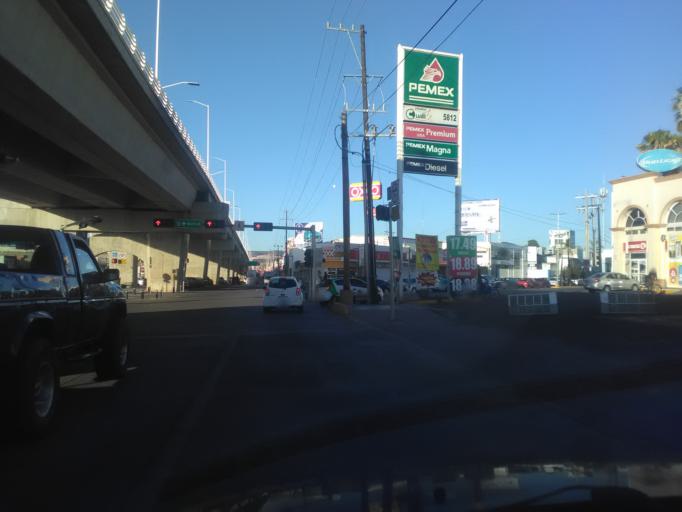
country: MX
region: Durango
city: Victoria de Durango
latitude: 24.0103
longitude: -104.6924
